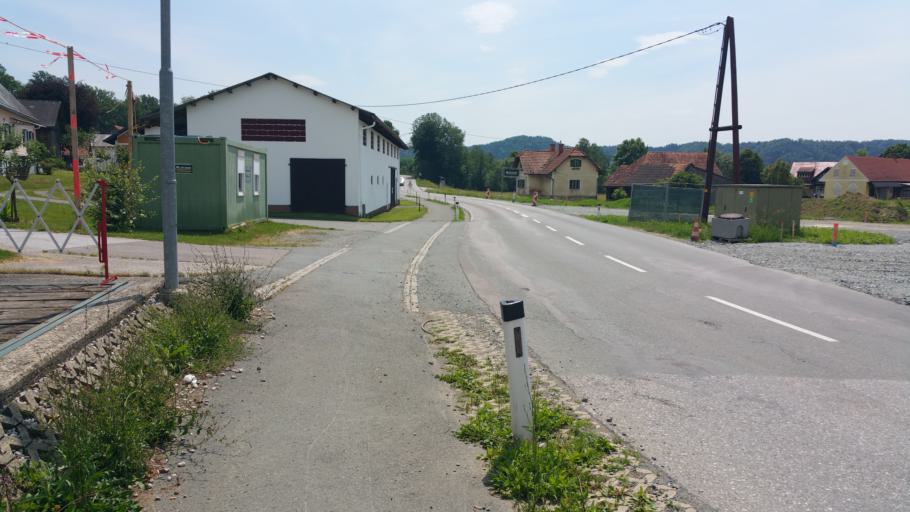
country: AT
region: Styria
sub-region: Politischer Bezirk Deutschlandsberg
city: Sankt Martin im Sulmtal
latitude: 46.7502
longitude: 15.3299
